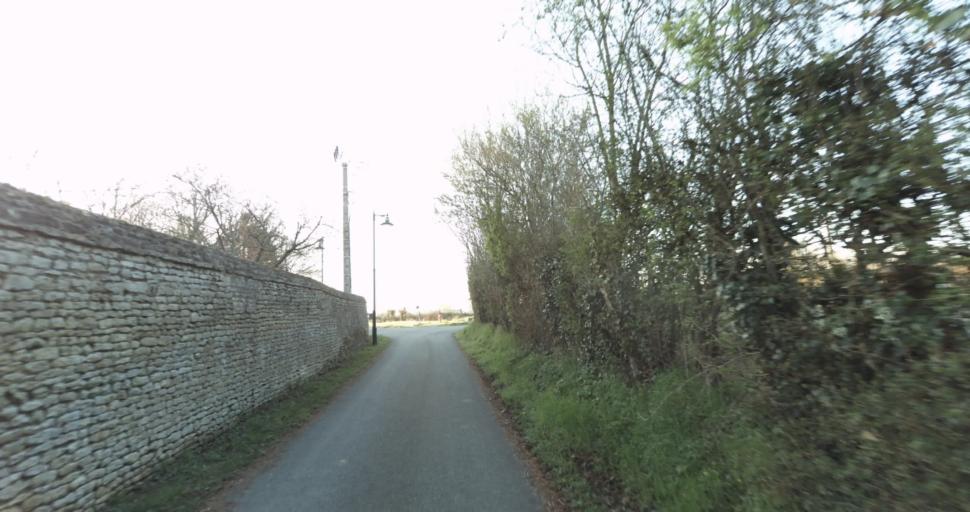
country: FR
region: Lower Normandy
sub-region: Departement du Calvados
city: Saint-Pierre-sur-Dives
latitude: 49.0228
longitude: -0.0094
